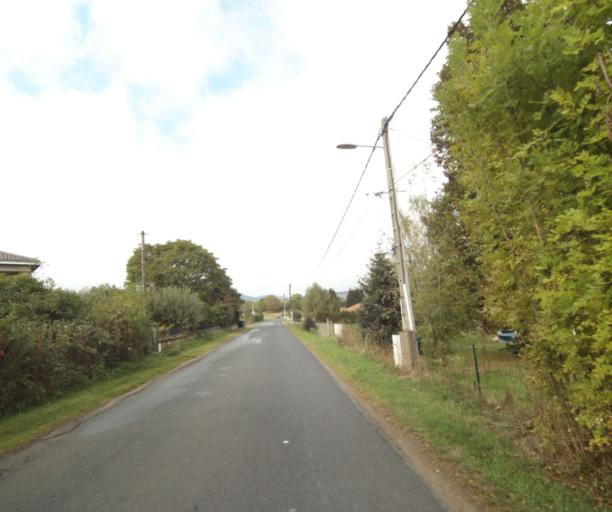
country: FR
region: Auvergne
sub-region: Departement du Puy-de-Dome
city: Saint-Genes-Champanelle
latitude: 45.7073
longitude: 3.0028
